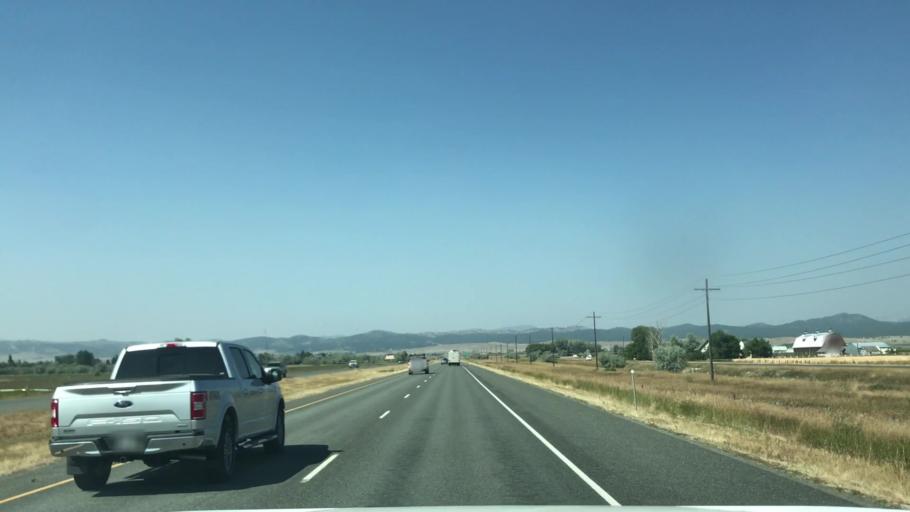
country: US
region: Montana
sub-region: Lewis and Clark County
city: Helena Valley West Central
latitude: 46.6786
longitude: -112.0115
